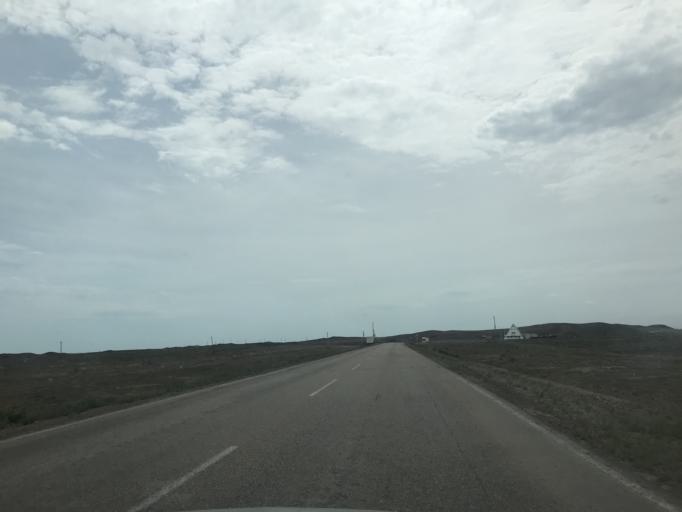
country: KZ
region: Zhambyl
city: Mynaral
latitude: 45.4530
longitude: 73.5973
